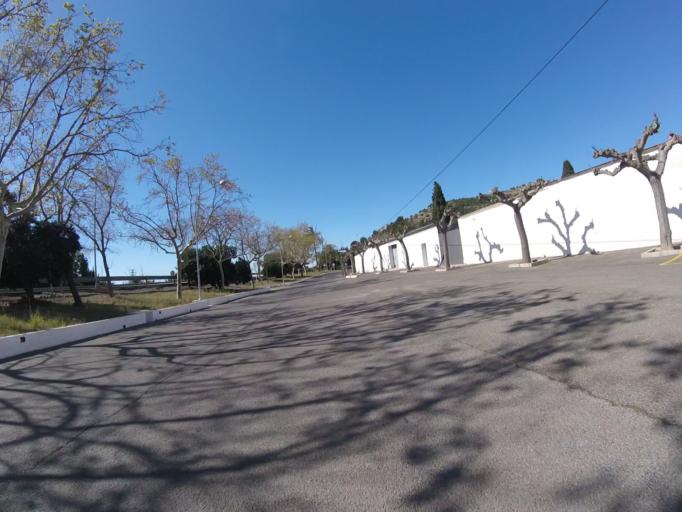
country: ES
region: Valencia
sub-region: Provincia de Castello
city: Benicassim
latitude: 40.0611
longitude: 0.0700
